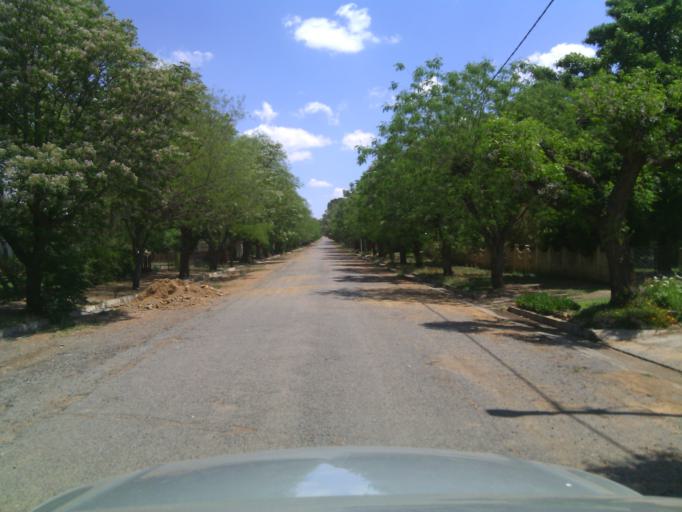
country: ZA
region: Orange Free State
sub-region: Xhariep District Municipality
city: Dewetsdorp
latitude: -29.5780
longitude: 26.6670
